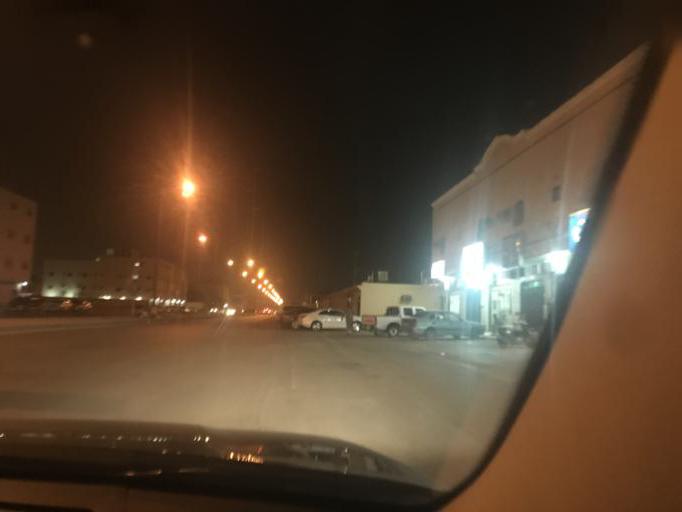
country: SA
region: Ar Riyad
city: Riyadh
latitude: 24.8232
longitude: 46.7408
